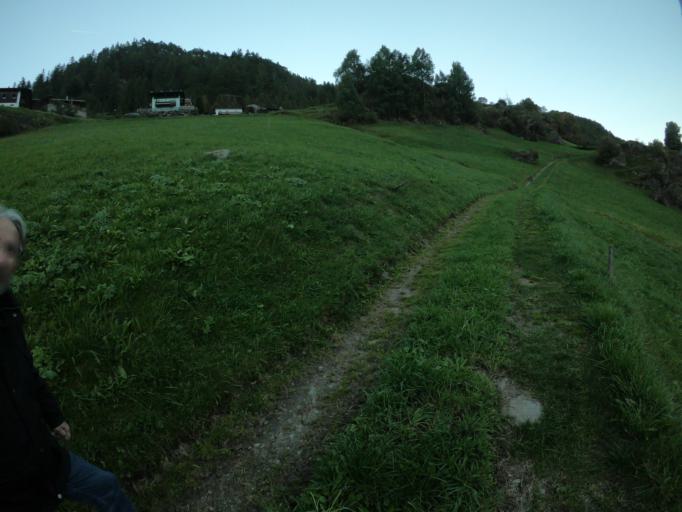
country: AT
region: Tyrol
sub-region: Politischer Bezirk Imst
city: Soelden
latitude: 46.9648
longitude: 11.0110
